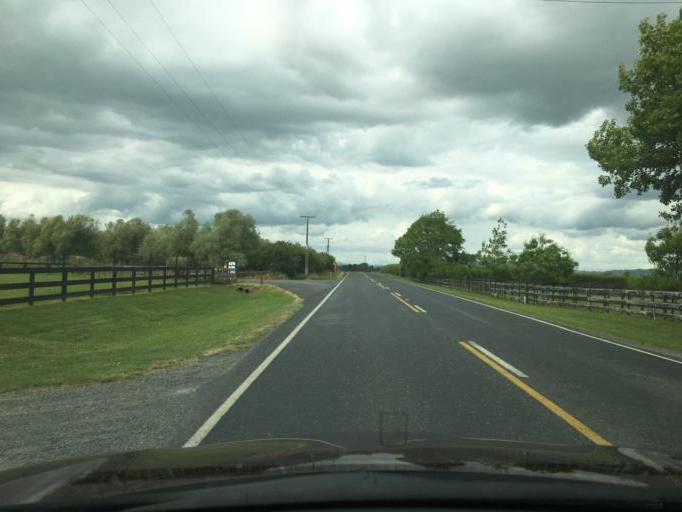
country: NZ
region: Waikato
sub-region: Waipa District
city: Cambridge
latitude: -38.0011
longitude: 175.3918
